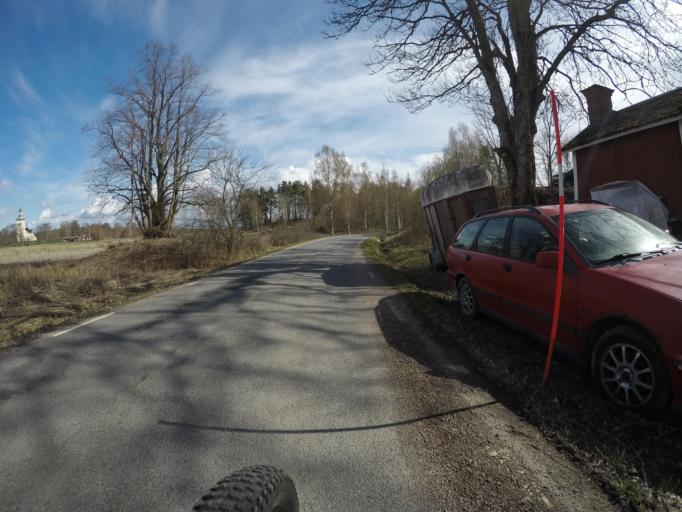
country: SE
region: Vaestmanland
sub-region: Kungsors Kommun
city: Kungsoer
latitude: 59.2864
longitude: 16.1523
